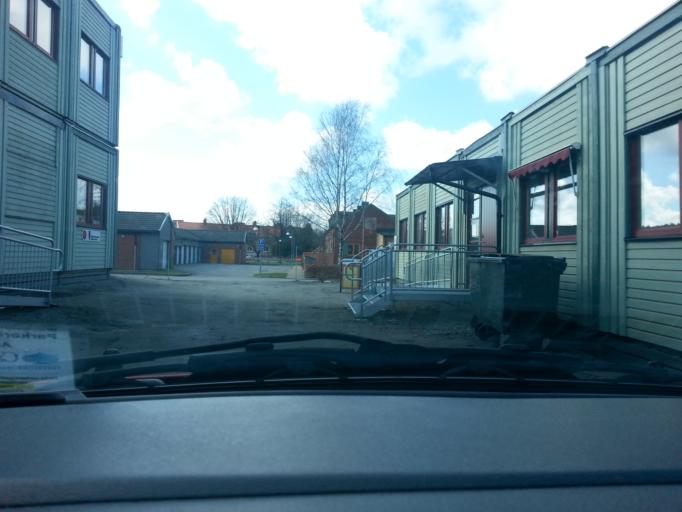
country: SE
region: Vaestra Goetaland
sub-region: Partille Kommun
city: Partille
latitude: 57.7407
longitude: 12.1157
